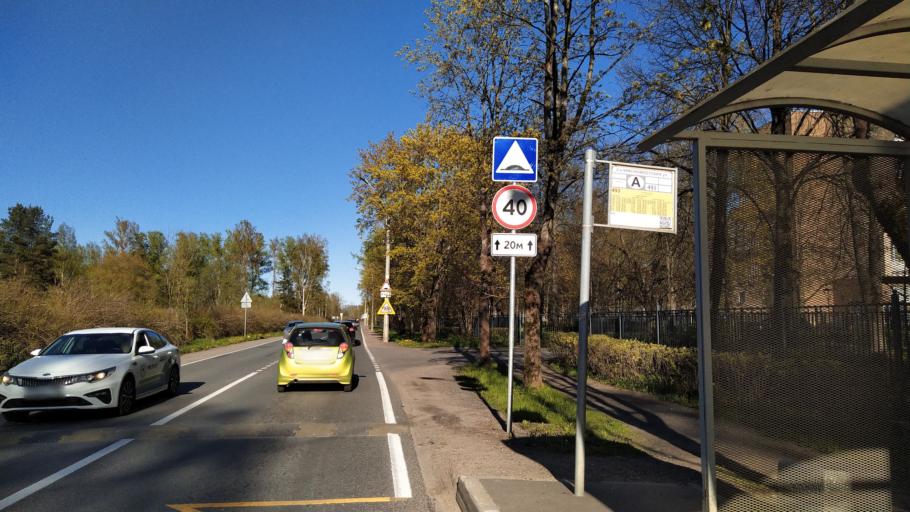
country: RU
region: St.-Petersburg
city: Tyarlevo
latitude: 59.6852
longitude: 30.4727
